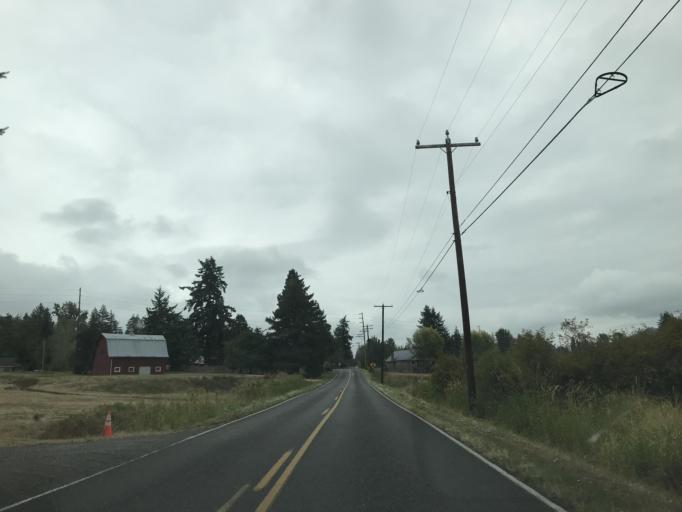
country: US
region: Washington
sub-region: Whatcom County
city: Sudden Valley
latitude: 48.8165
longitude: -122.3326
